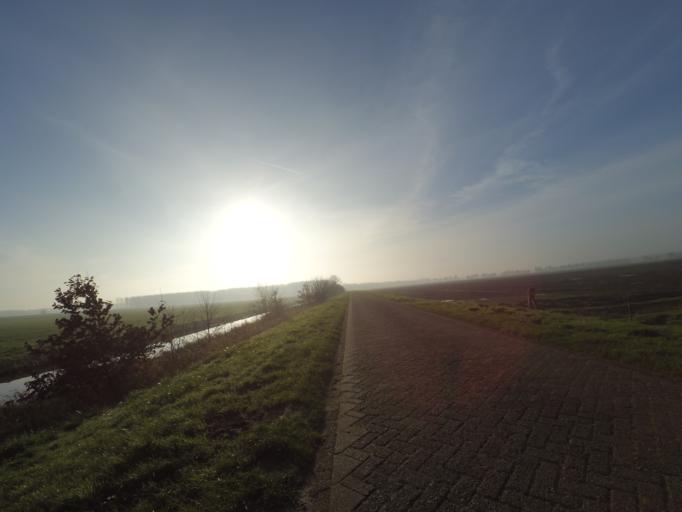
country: NL
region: Drenthe
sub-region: Gemeente Borger-Odoorn
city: Borger
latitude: 52.8982
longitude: 6.7609
